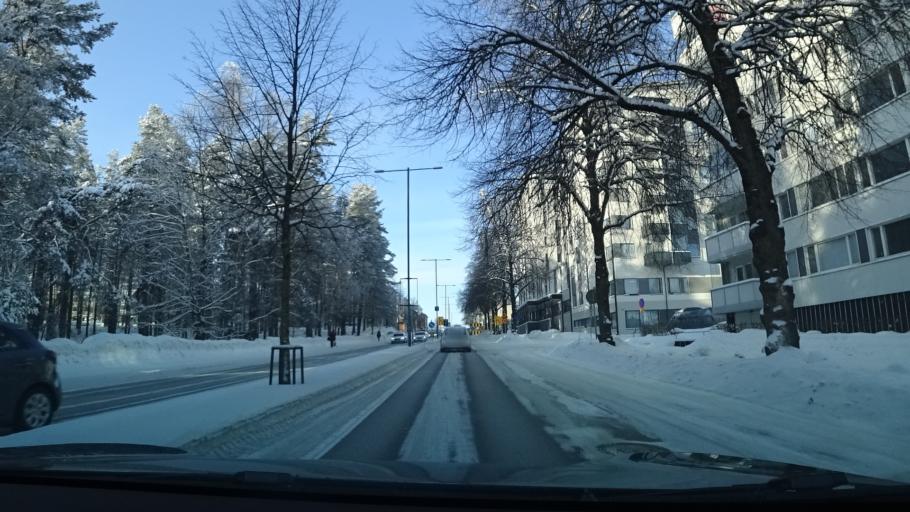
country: FI
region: South Karelia
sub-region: Lappeenranta
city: Lappeenranta
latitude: 61.0520
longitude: 28.1933
